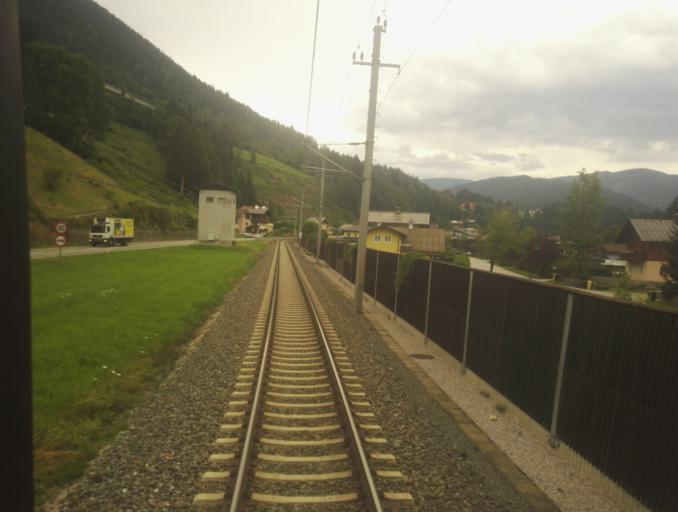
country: AT
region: Salzburg
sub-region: Politischer Bezirk Sankt Johann im Pongau
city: Huttau
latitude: 47.4196
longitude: 13.3283
